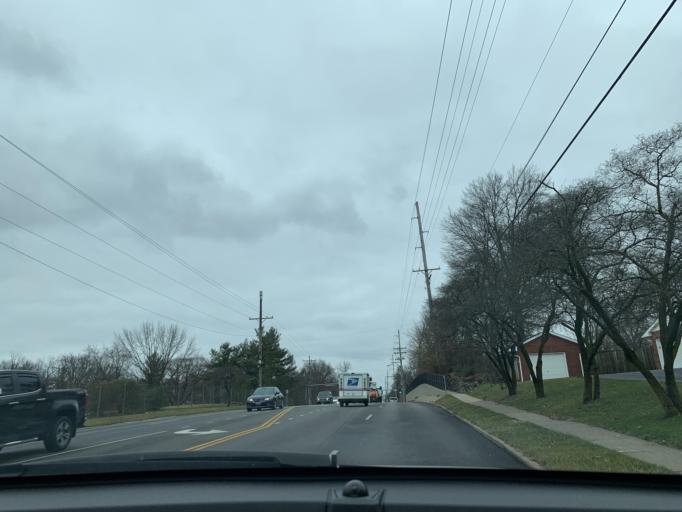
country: US
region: Illinois
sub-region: Sangamon County
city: Leland Grove
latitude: 39.7816
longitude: -89.6870
